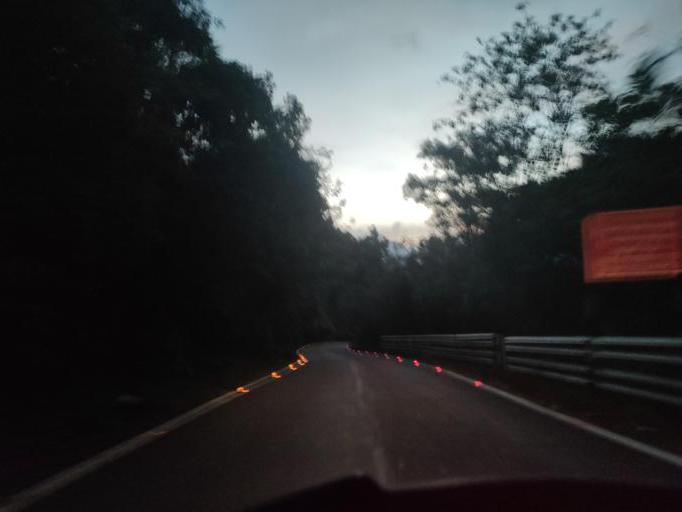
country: IN
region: Tamil Nadu
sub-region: Dindigul
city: Kodaikanal
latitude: 10.2822
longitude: 77.5370
